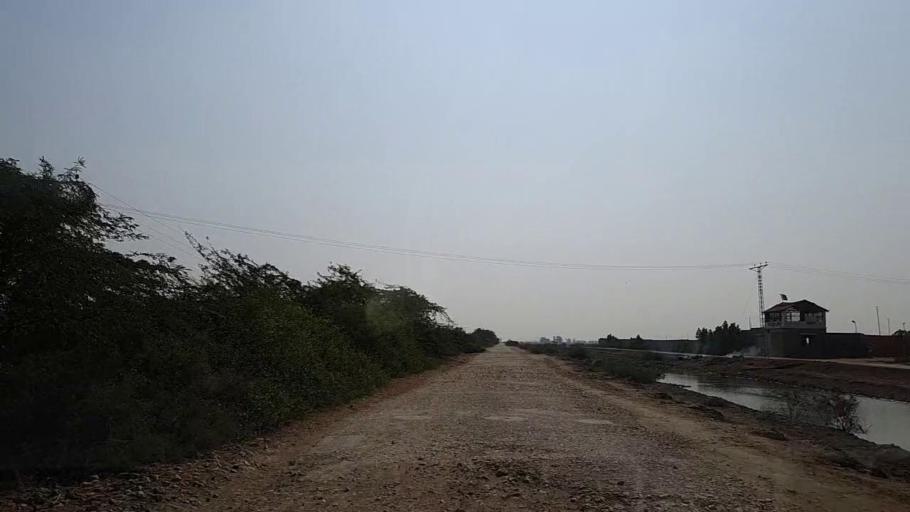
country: PK
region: Sindh
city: Thatta
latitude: 24.7211
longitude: 67.7684
